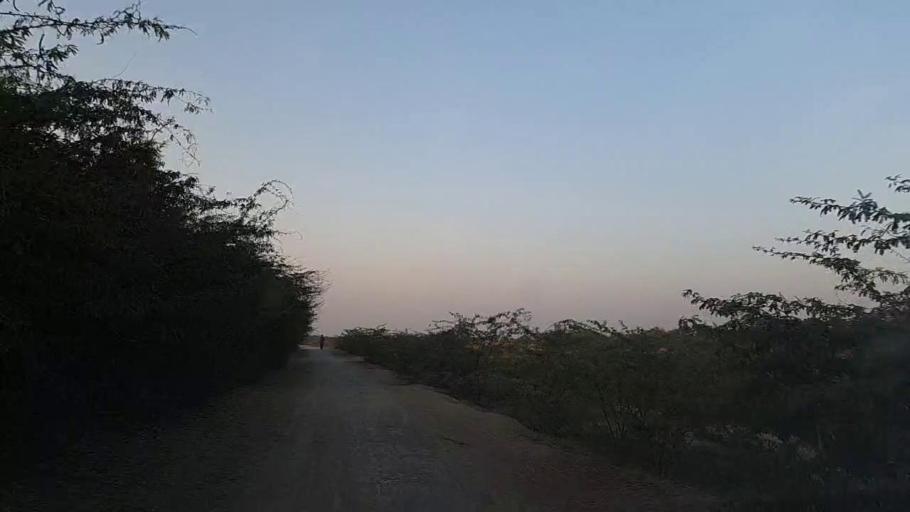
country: PK
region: Sindh
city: Naukot
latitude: 24.9507
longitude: 69.4284
